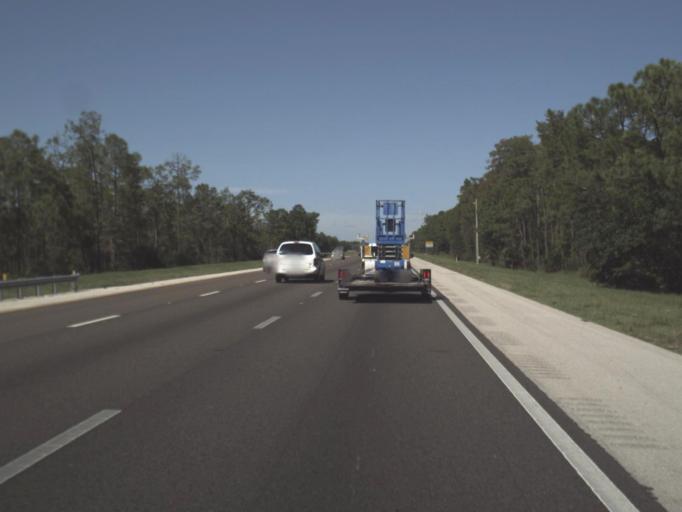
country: US
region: Florida
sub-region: Lee County
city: Gateway
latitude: 26.5790
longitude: -81.7931
